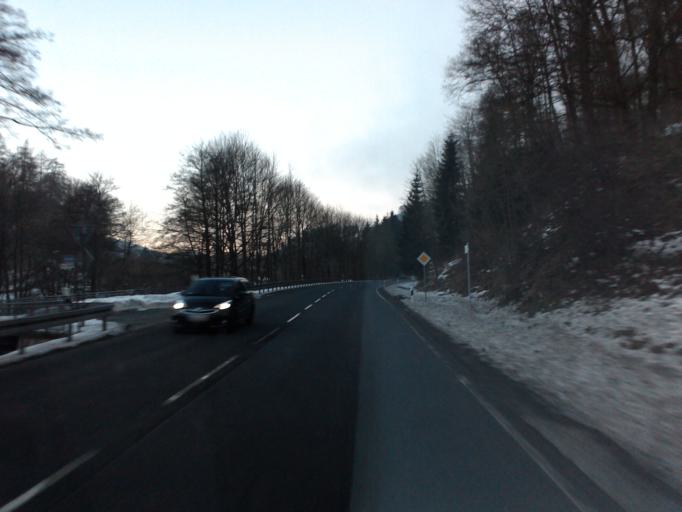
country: DE
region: North Rhine-Westphalia
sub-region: Regierungsbezirk Arnsberg
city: Winterberg
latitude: 51.2656
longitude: 8.5238
